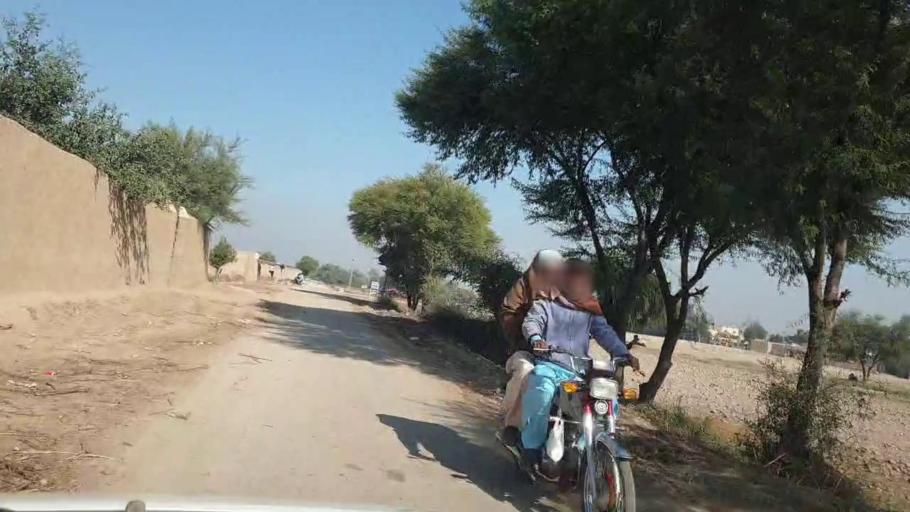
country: PK
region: Sindh
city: Bhan
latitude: 26.6094
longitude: 67.7343
